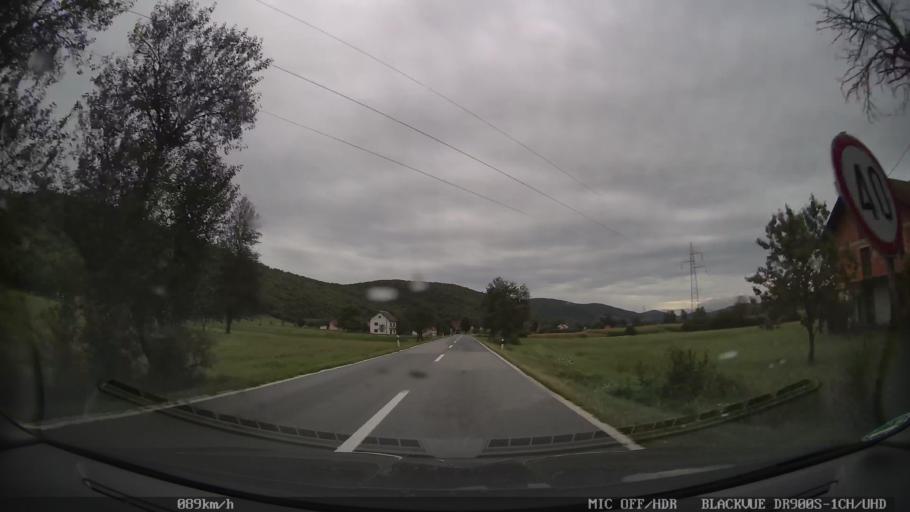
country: HR
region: Licko-Senjska
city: Brinje
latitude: 44.9195
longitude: 15.1486
